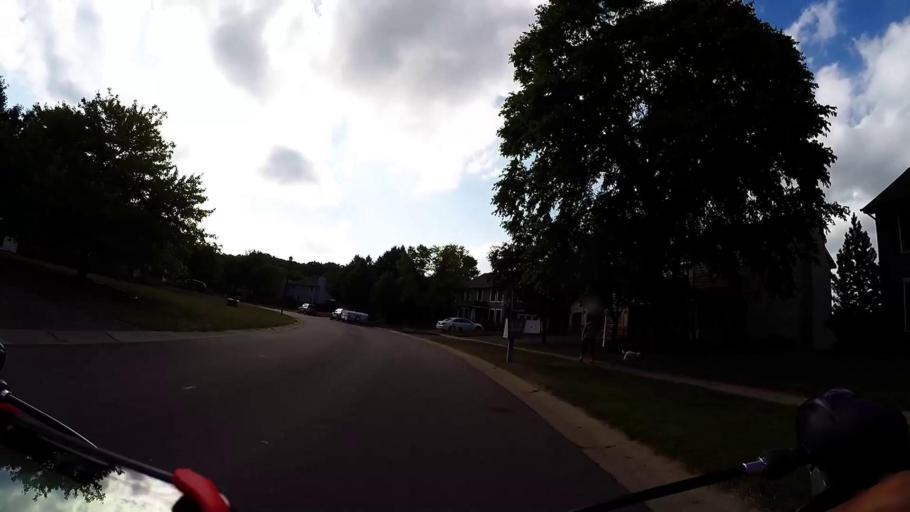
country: US
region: Minnesota
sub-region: Hennepin County
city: Minnetonka
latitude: 44.8865
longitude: -93.4850
